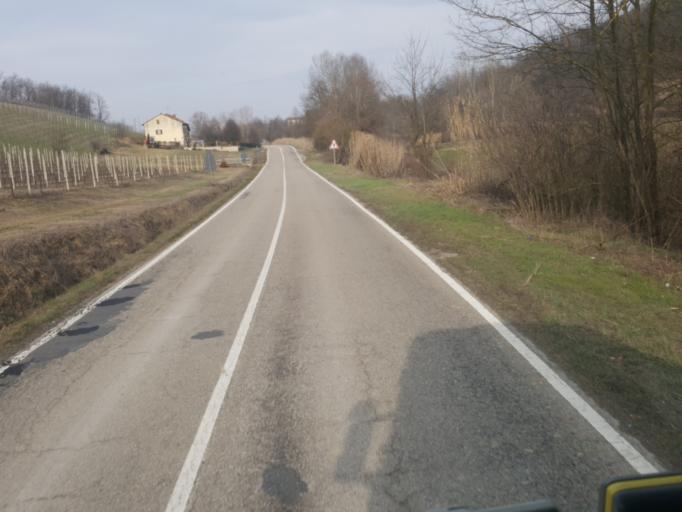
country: IT
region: Piedmont
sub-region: Provincia di Asti
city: Castelnuovo Belbo
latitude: 44.7907
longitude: 8.4228
